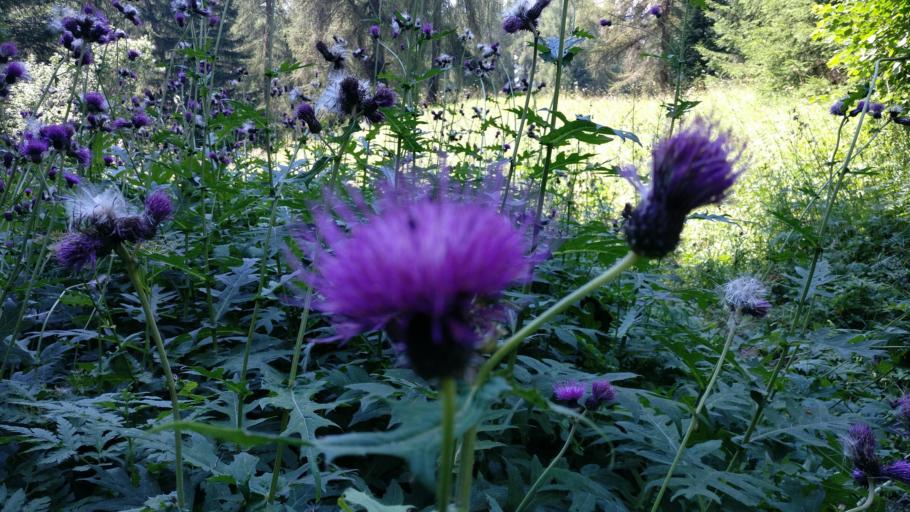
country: IT
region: Trentino-Alto Adige
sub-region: Provincia di Trento
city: Ruffre
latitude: 46.4364
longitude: 11.1879
